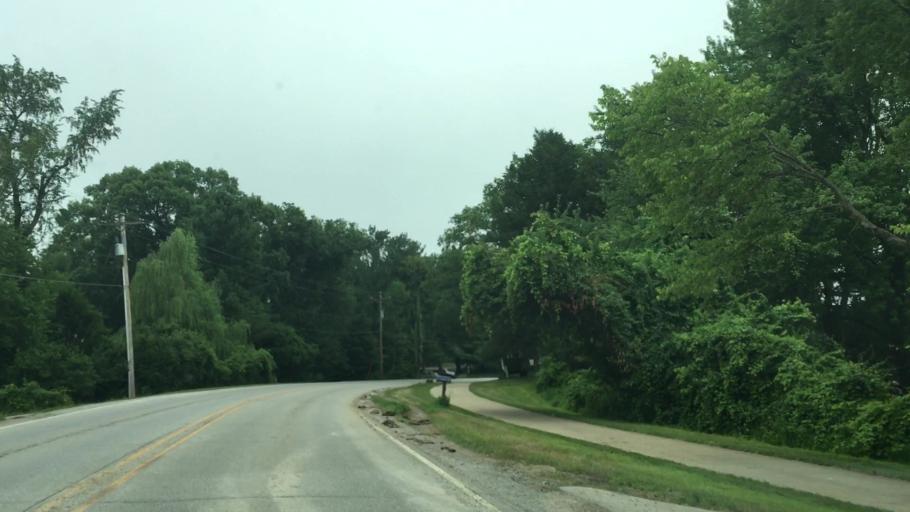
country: US
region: Iowa
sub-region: Johnson County
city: Coralville
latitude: 41.7036
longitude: -91.5454
